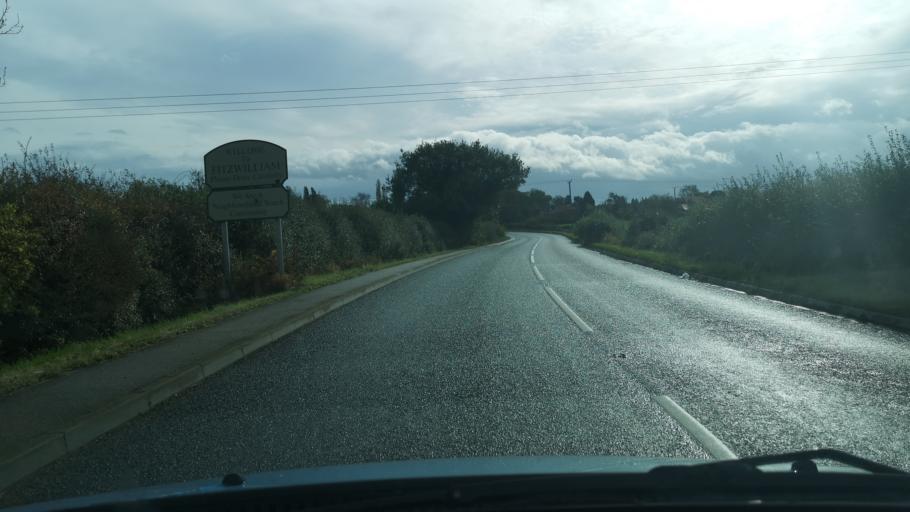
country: GB
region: England
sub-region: City and Borough of Wakefield
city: Fitzwilliam
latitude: 53.6402
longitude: -1.3831
